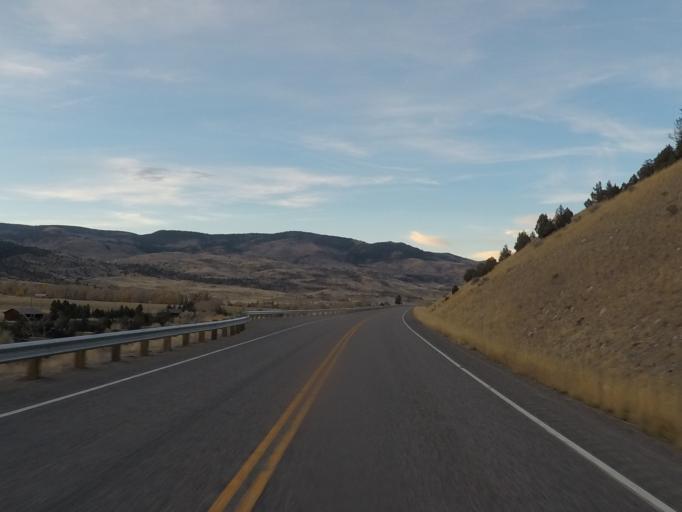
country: US
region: Montana
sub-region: Gallatin County
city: Big Sky
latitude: 45.1932
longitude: -110.8995
